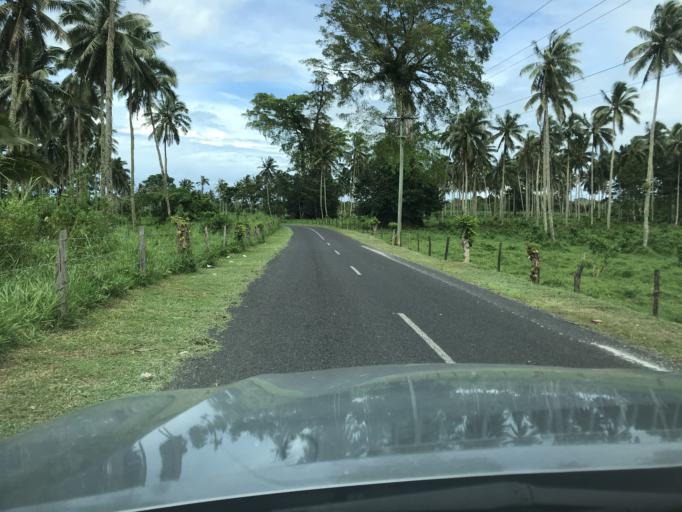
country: WS
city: Fasito`outa
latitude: -13.8708
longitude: -171.9137
